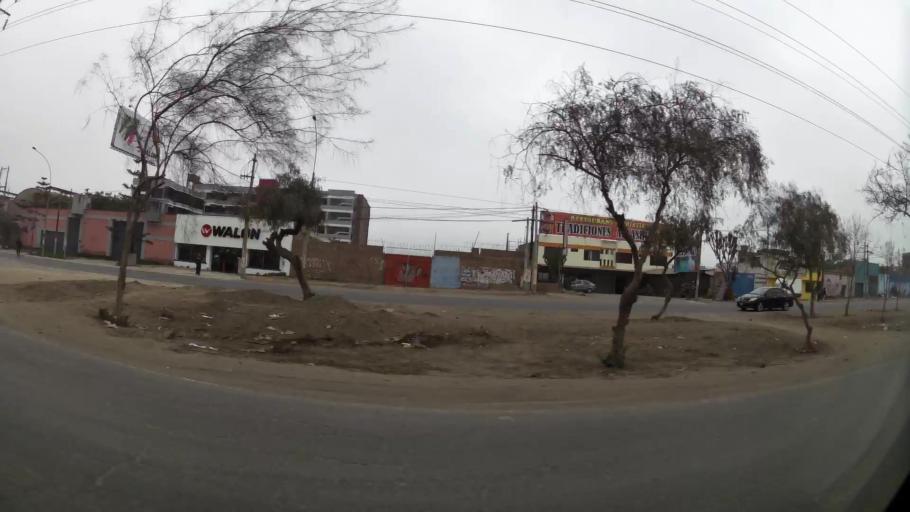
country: PE
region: Lima
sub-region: Lima
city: Urb. Santo Domingo
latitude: -11.9246
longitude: -77.0636
